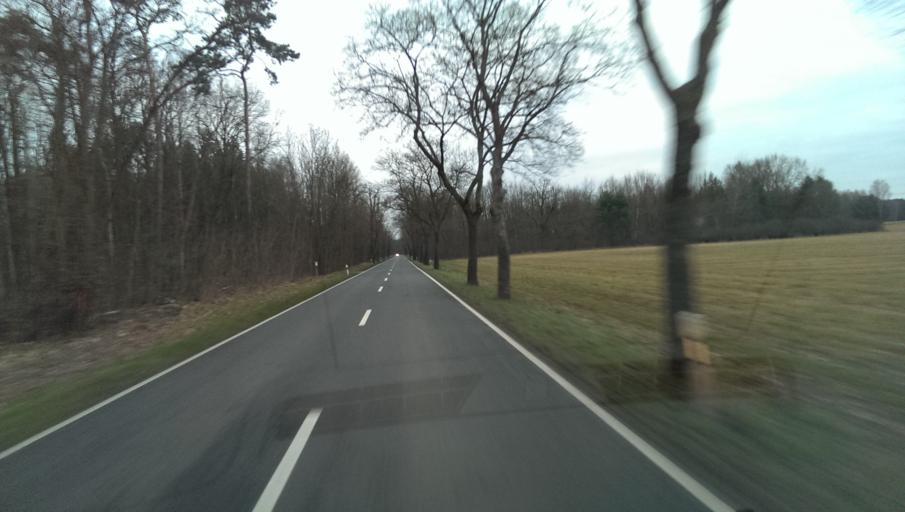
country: DE
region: Brandenburg
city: Sperenberg
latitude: 52.1493
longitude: 13.3565
